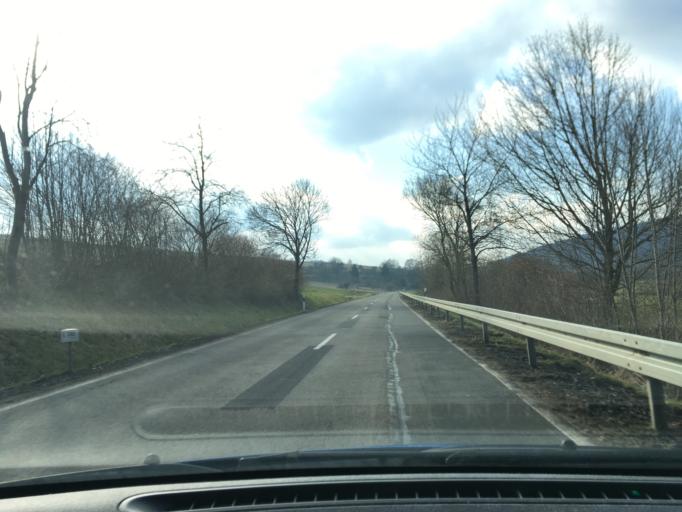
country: DE
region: Lower Saxony
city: Uslar
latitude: 51.6227
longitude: 9.6359
